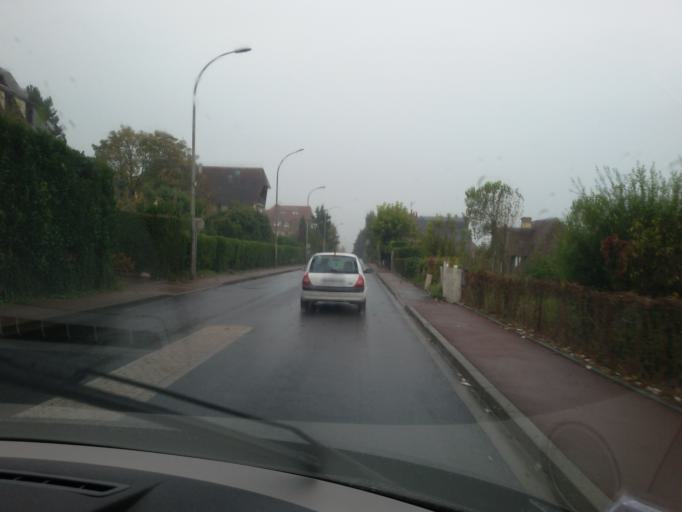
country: FR
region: Lower Normandy
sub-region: Departement du Calvados
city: Blonville-sur-Mer
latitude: 49.3432
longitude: 0.0365
